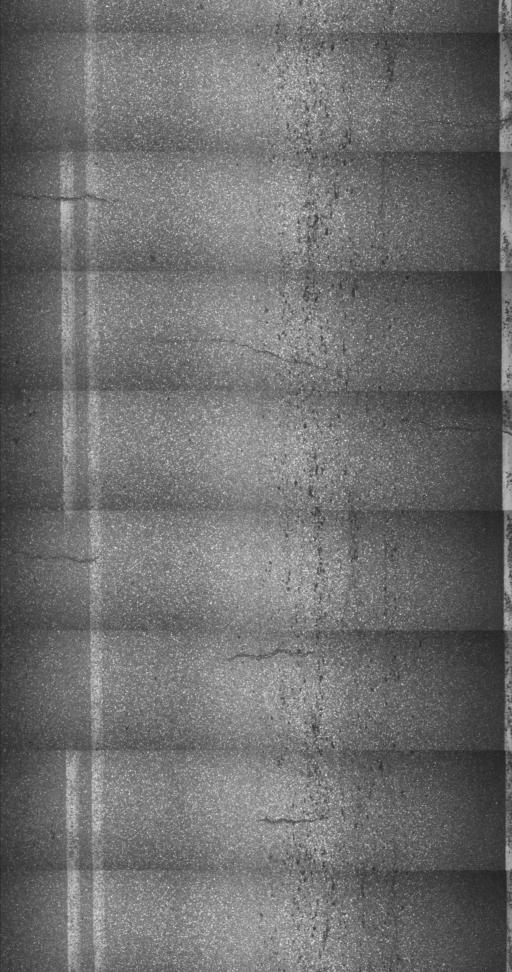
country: US
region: Vermont
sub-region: Orleans County
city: Newport
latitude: 44.8919
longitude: -72.0563
